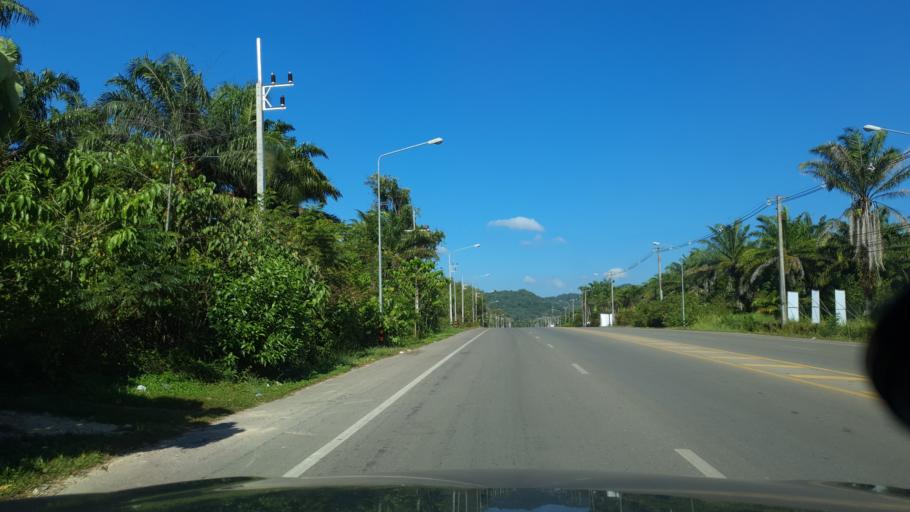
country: TH
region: Phangnga
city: Ban Ao Nang
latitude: 8.0374
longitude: 98.8543
